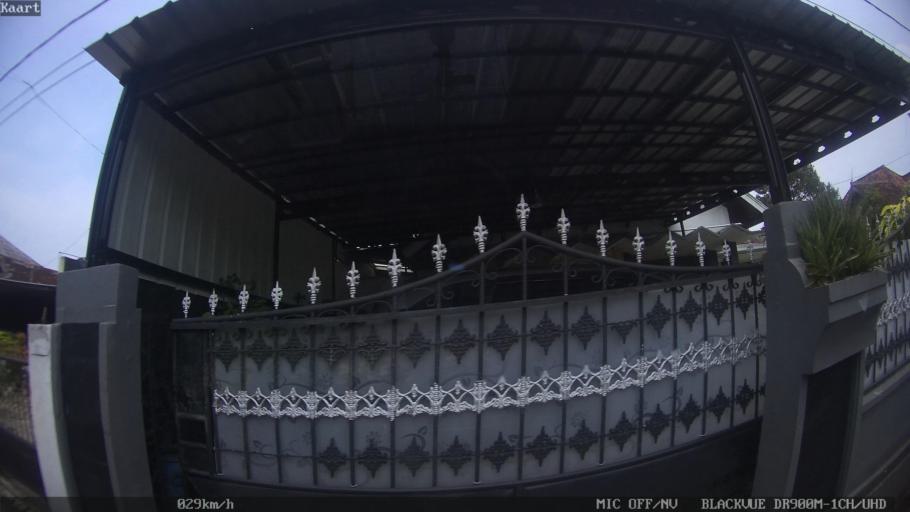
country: ID
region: Lampung
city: Bandarlampung
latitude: -5.4153
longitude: 105.2638
